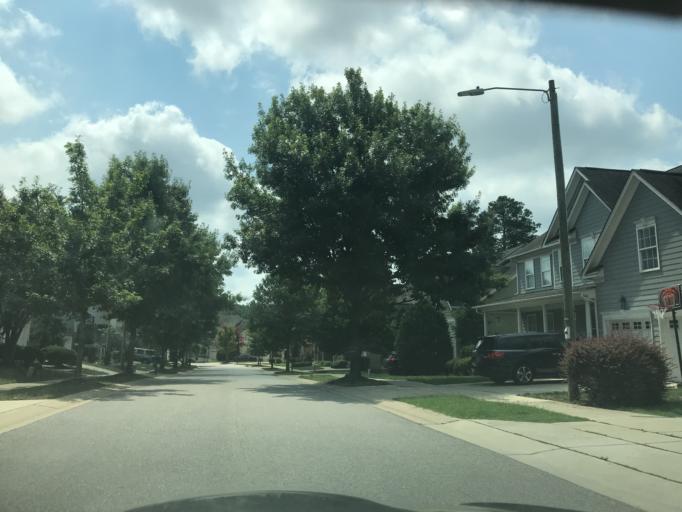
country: US
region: North Carolina
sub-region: Wake County
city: Wake Forest
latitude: 35.9215
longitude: -78.5623
